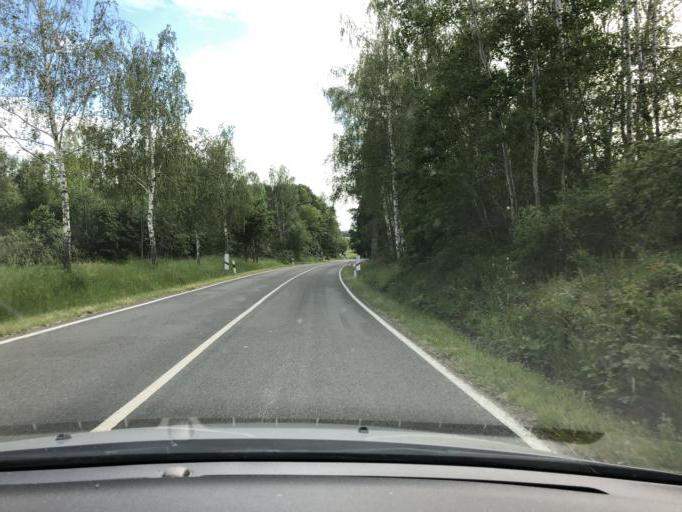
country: DE
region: Saxony
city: Trebsen
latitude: 51.2833
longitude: 12.7351
